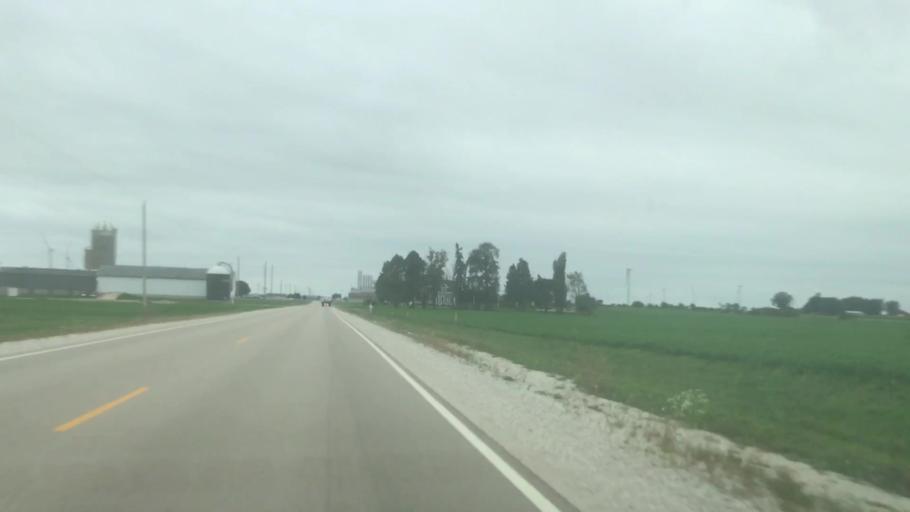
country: US
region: Wisconsin
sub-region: Fond du Lac County
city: Oakfield
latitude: 43.6231
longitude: -88.5417
